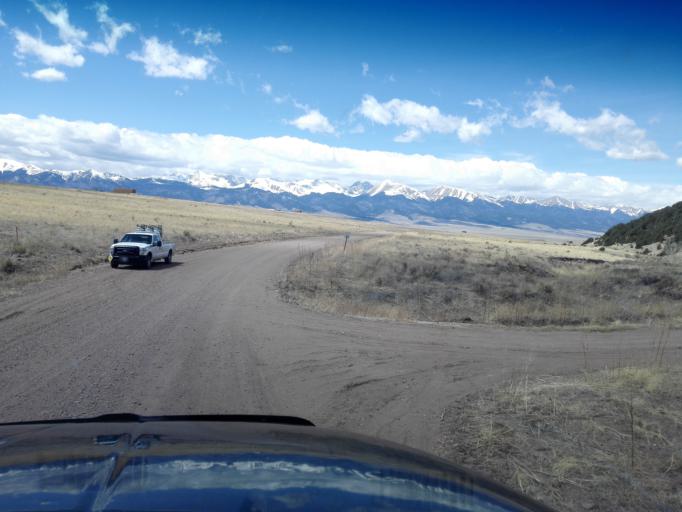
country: US
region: Colorado
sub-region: Custer County
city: Westcliffe
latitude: 37.9843
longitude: -105.3071
